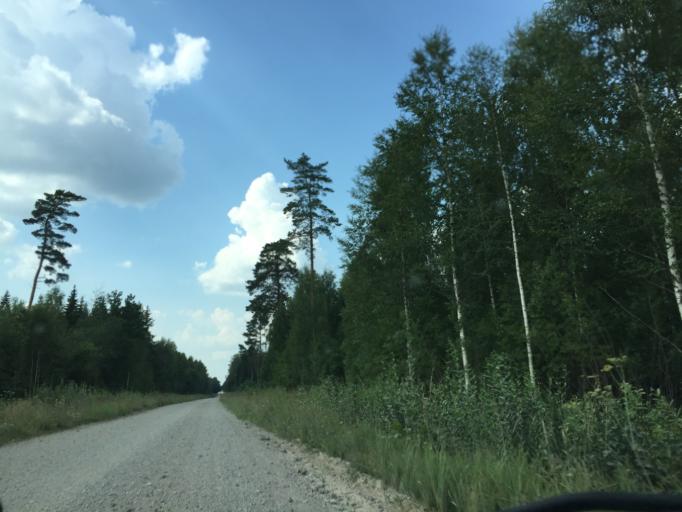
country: LV
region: Auces Novads
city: Auce
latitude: 56.4154
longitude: 22.9851
